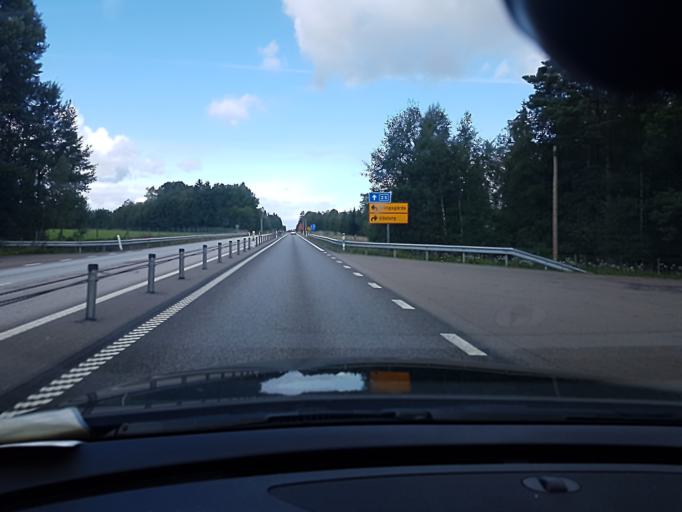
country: SE
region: Kronoberg
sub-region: Lessebo Kommun
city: Hovmantorp
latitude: 56.8166
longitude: 15.0983
